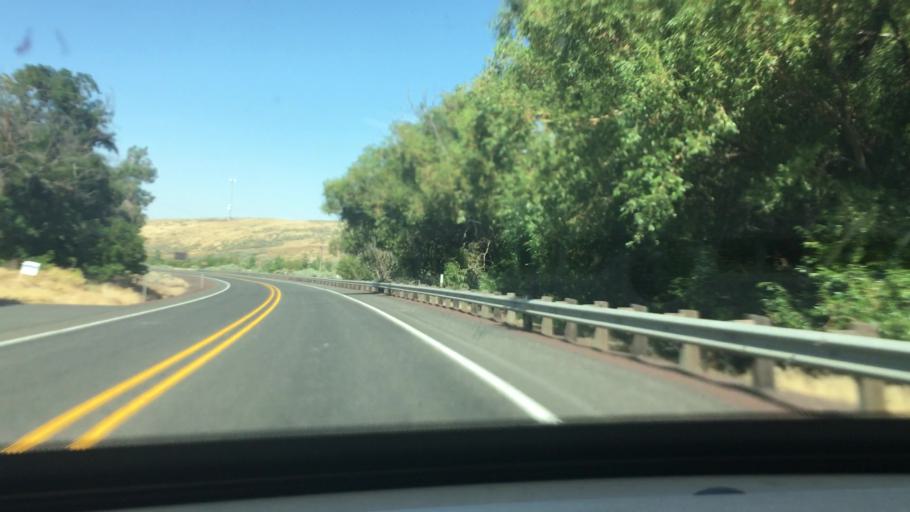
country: US
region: Oregon
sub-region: Sherman County
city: Moro
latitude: 45.5059
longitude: -120.6893
